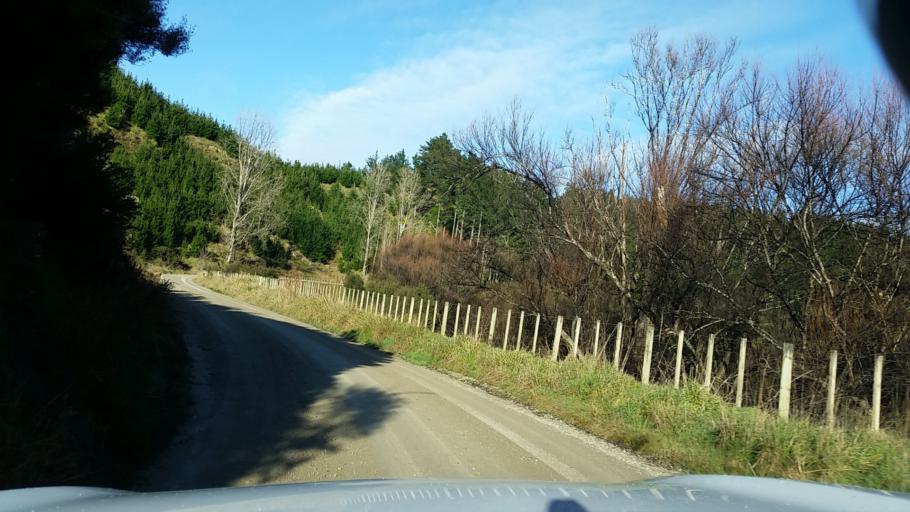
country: NZ
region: Taranaki
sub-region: South Taranaki District
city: Patea
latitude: -39.6983
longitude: 174.7393
